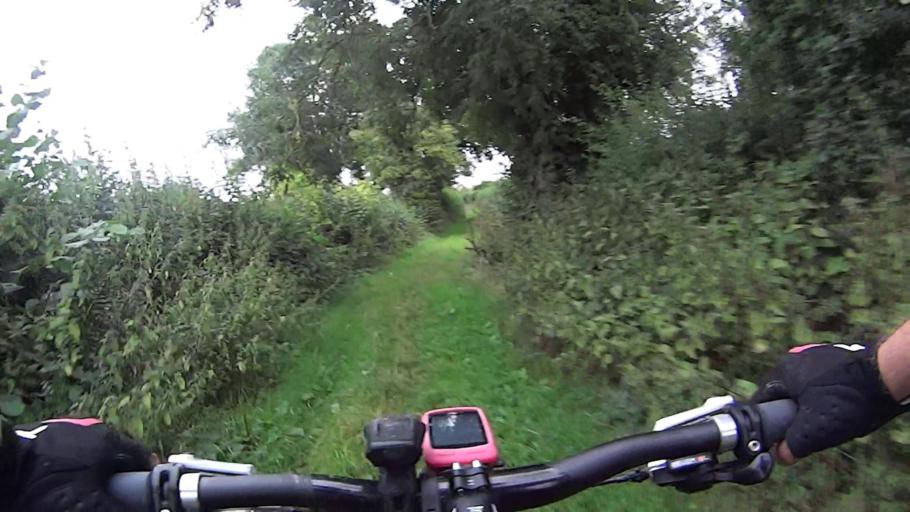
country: GB
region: England
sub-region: Worcestershire
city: Tenbury Wells
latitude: 52.3004
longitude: -2.6018
